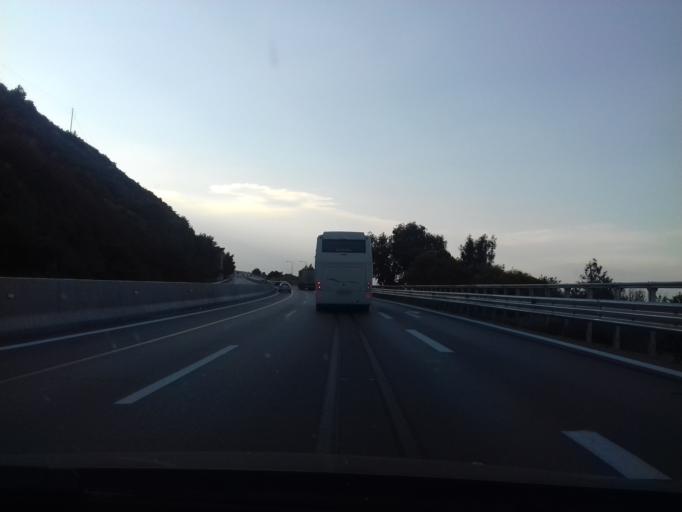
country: GR
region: West Greece
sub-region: Nomos Achaias
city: Siliveniotika
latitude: 38.1641
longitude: 22.3344
